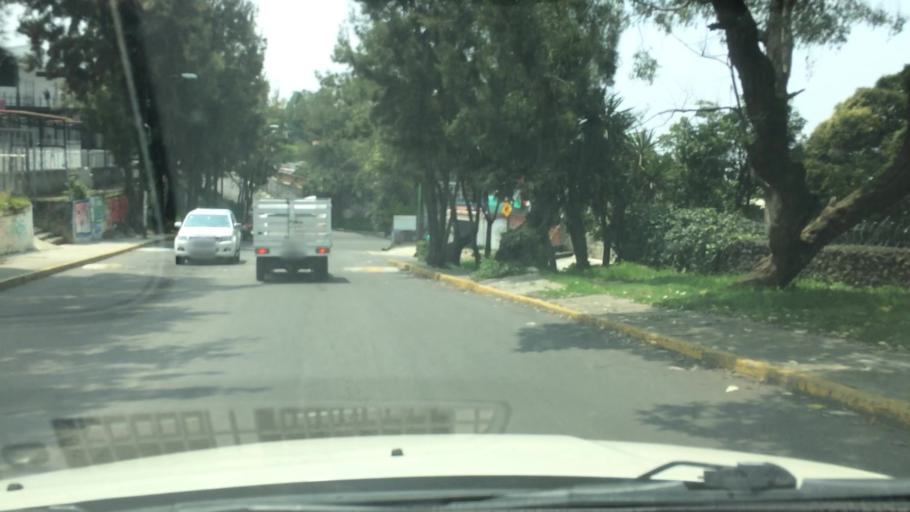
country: MX
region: Mexico City
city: Xochimilco
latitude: 19.2342
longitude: -99.1586
